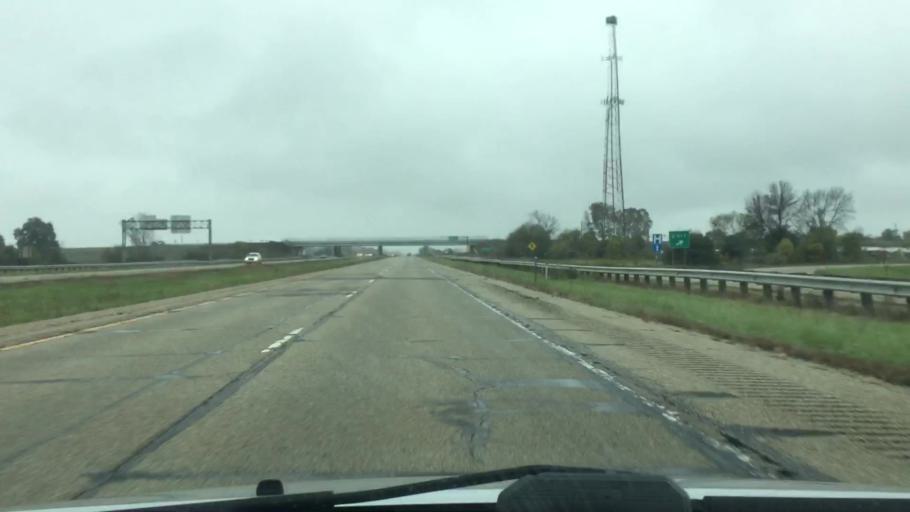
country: US
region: Wisconsin
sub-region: Walworth County
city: Elkhorn
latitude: 42.6734
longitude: -88.5213
